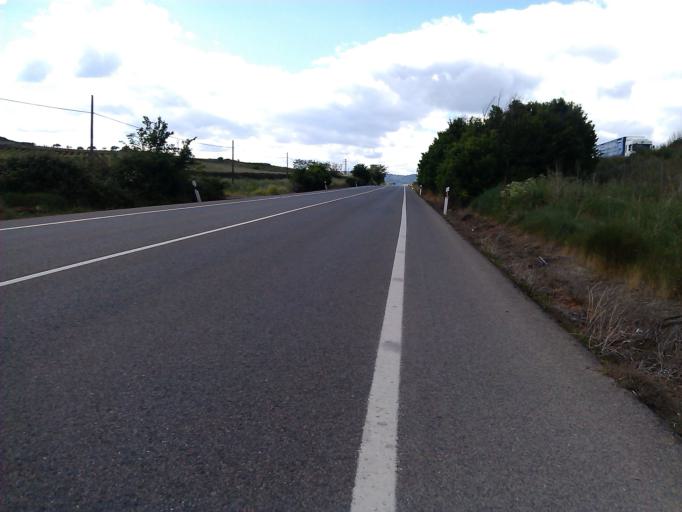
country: ES
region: La Rioja
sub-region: Provincia de La Rioja
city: Najera
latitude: 42.4281
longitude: -2.7493
